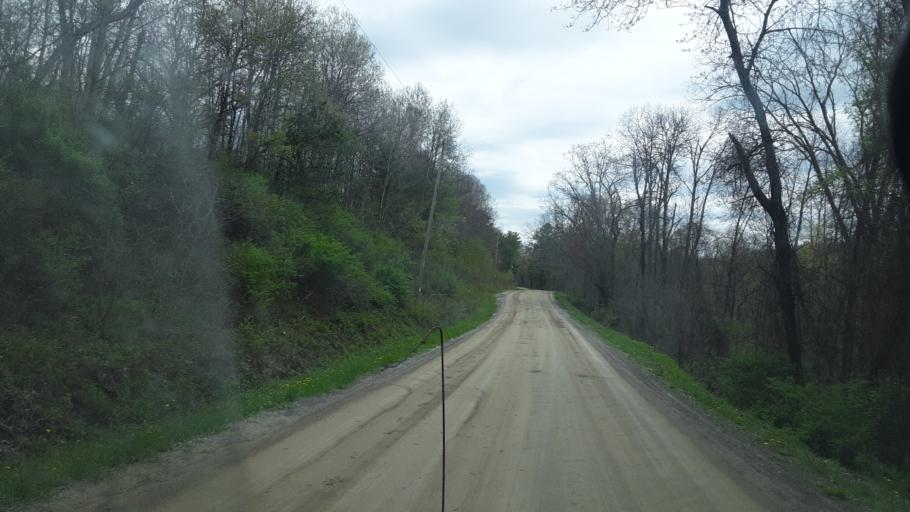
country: US
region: New York
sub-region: Steuben County
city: Addison
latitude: 42.0972
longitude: -77.3308
